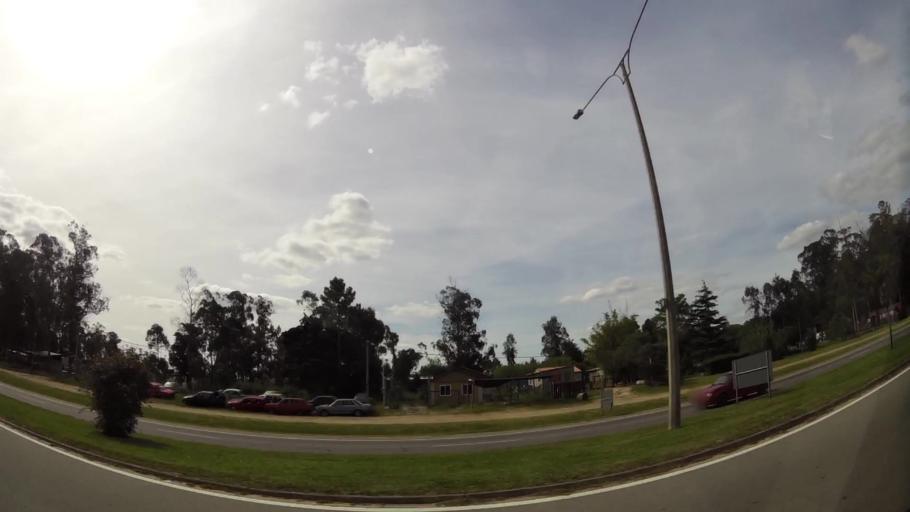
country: UY
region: Canelones
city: Empalme Olmos
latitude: -34.7832
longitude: -55.8838
